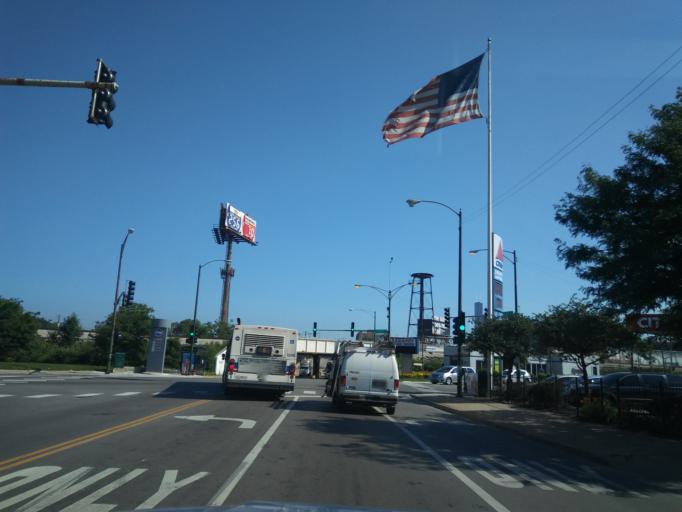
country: US
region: Illinois
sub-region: Cook County
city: Chicago
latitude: 41.8468
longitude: -87.6464
